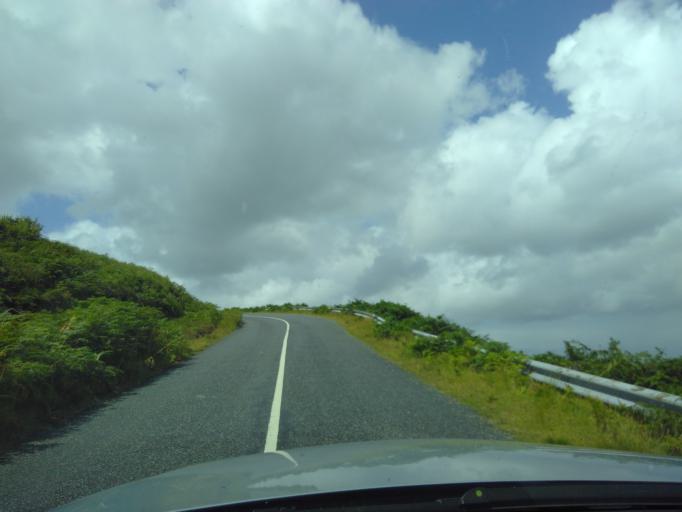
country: IE
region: Ulster
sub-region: County Donegal
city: Buncrana
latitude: 55.1863
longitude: -7.5885
